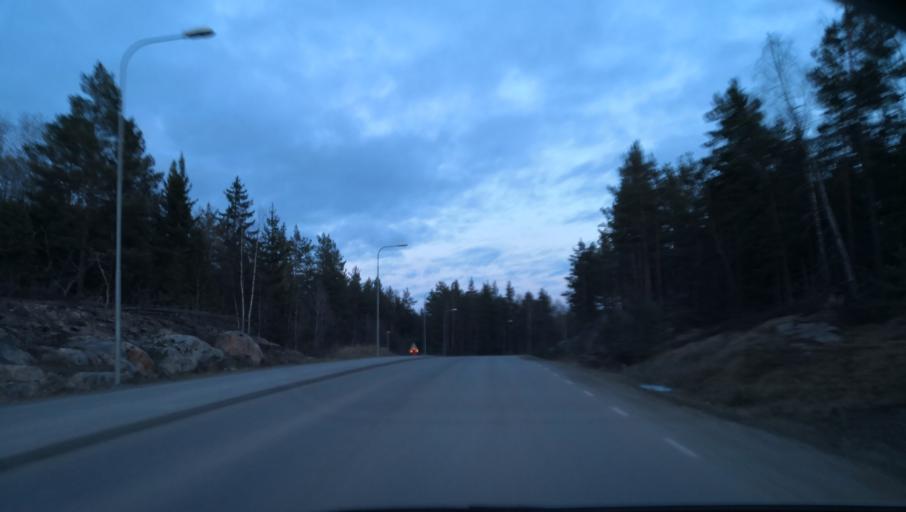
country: SE
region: Stockholm
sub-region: Nacka Kommun
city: Boo
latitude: 59.3415
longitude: 18.2949
